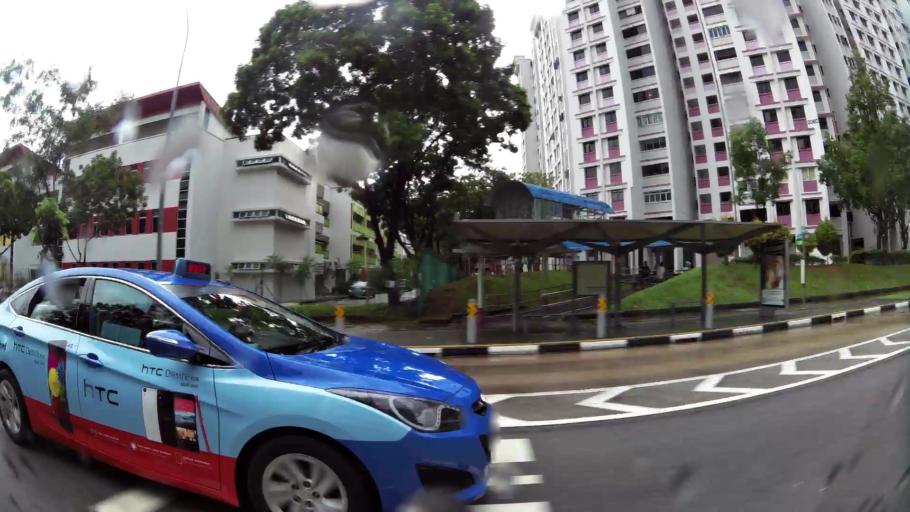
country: MY
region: Johor
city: Kampung Pasir Gudang Baru
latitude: 1.3875
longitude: 103.8980
